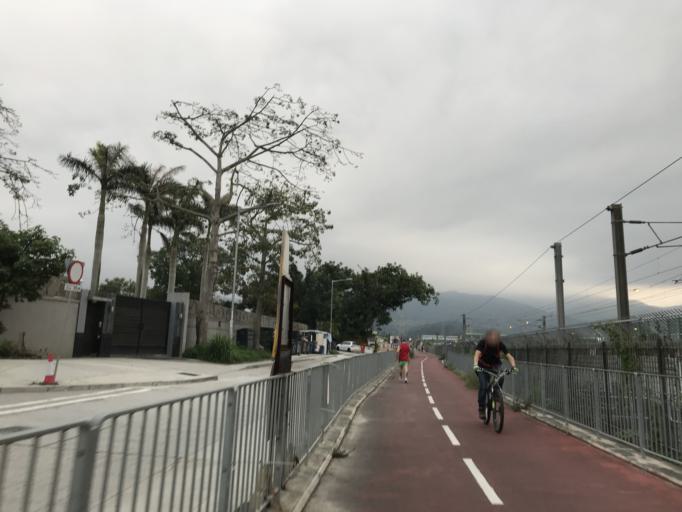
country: HK
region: Tai Po
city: Tai Po
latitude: 22.4741
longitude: 114.1542
